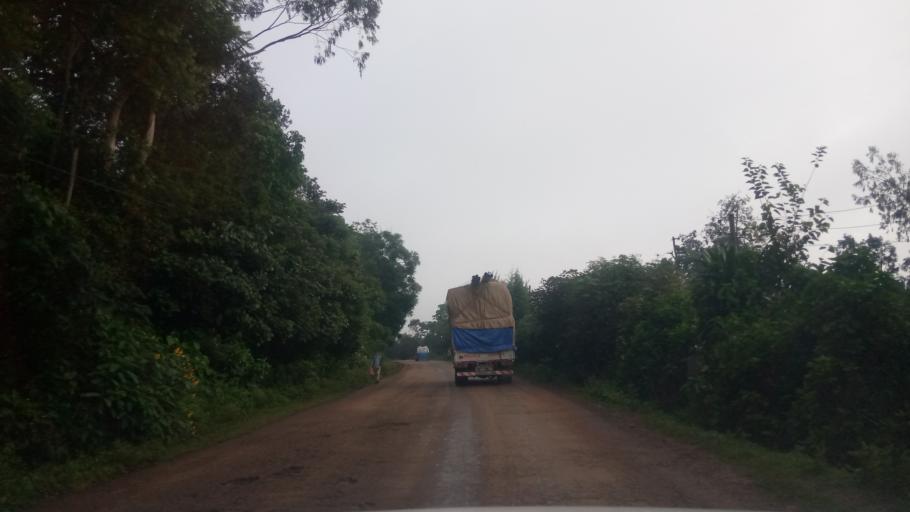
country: ET
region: Oromiya
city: Jima
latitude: 7.6906
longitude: 36.8254
